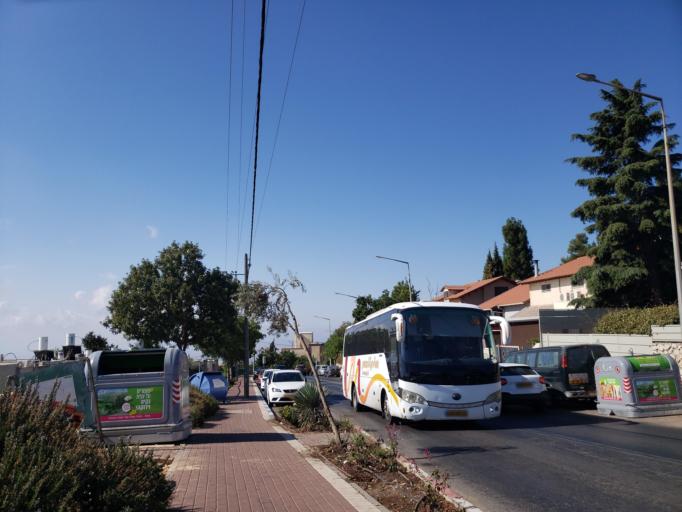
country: IL
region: Northern District
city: Safed
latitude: 32.9629
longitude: 35.4990
